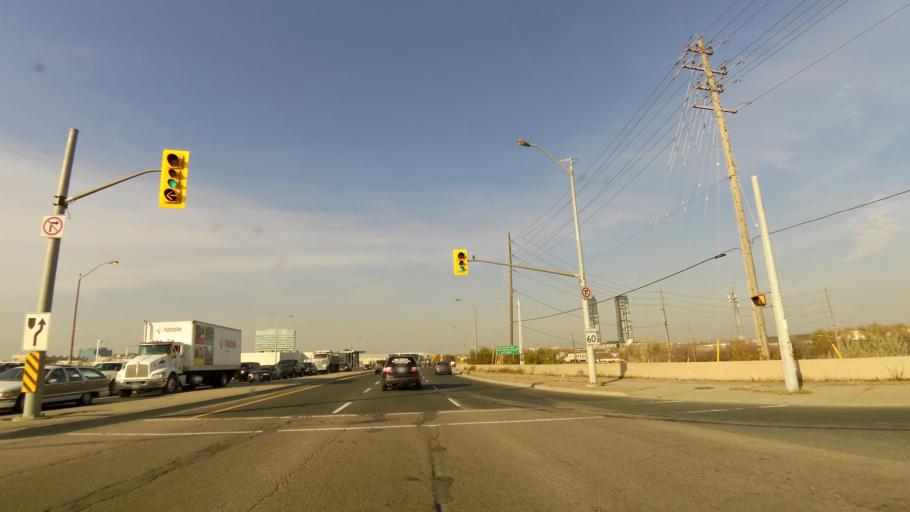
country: CA
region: Ontario
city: Concord
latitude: 43.7868
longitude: -79.5236
